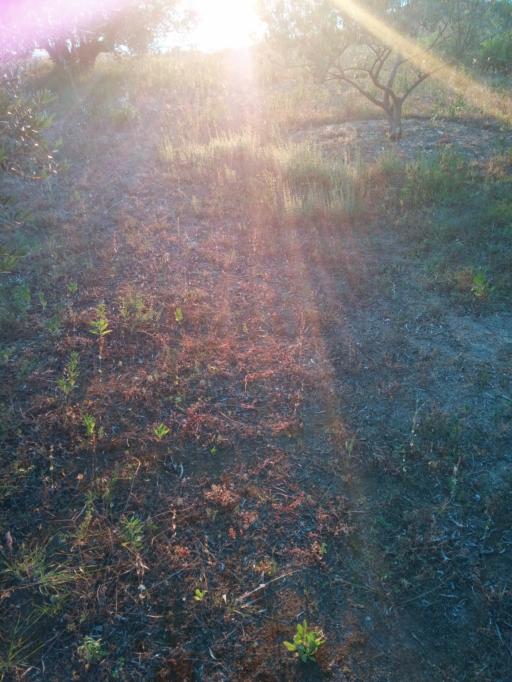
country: HR
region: Sibensko-Kniniska
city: Vodice
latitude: 43.7423
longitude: 15.7823
